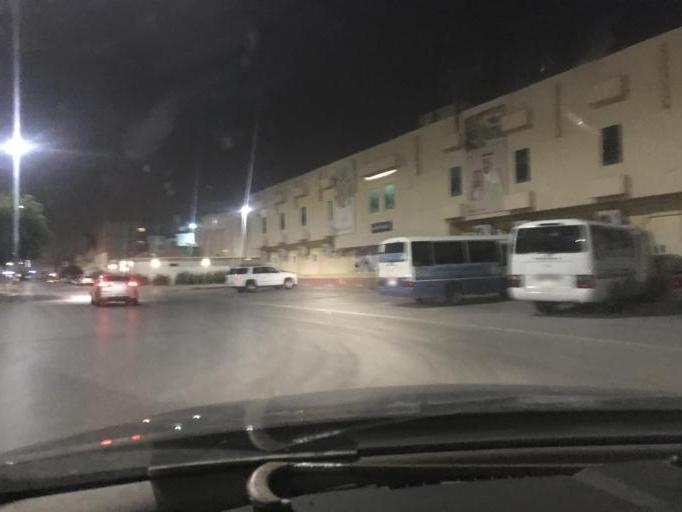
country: SA
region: Ar Riyad
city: Riyadh
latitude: 24.7311
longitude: 46.7777
